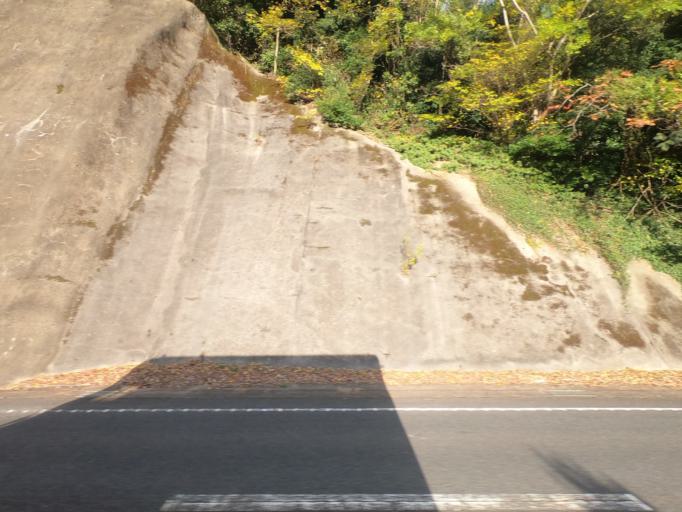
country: JP
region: Kumamoto
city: Minamata
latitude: 32.2447
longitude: 130.4784
